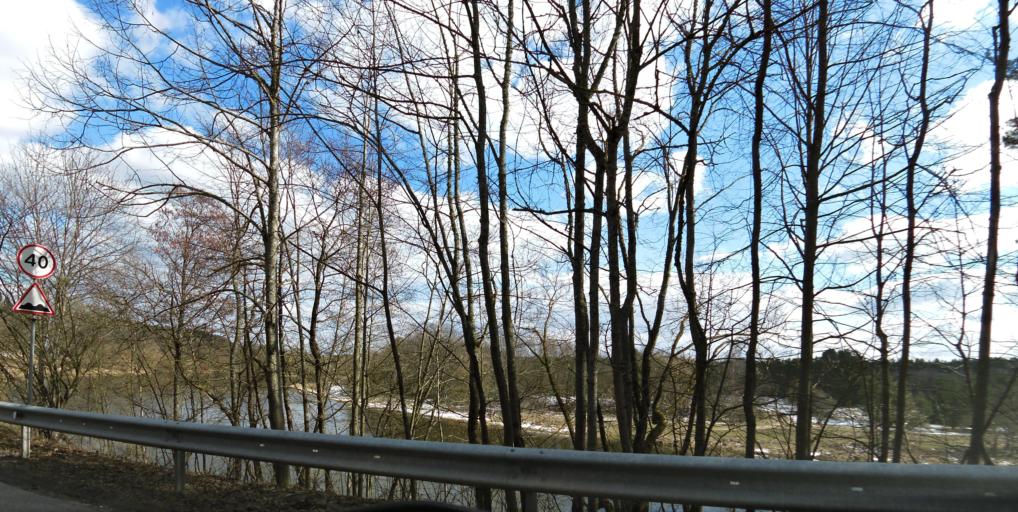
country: LT
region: Vilnius County
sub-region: Vilnius
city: Fabijoniskes
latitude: 54.7450
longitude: 25.2908
